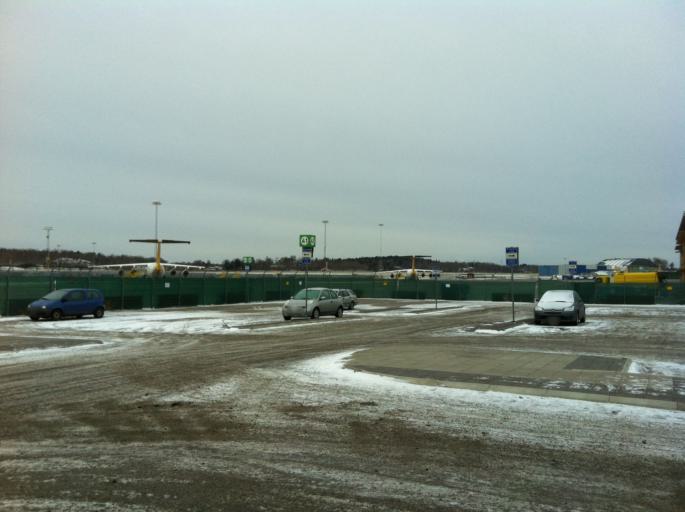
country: SE
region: Stockholm
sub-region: Stockholms Kommun
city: Bromma
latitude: 59.3574
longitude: 17.9477
